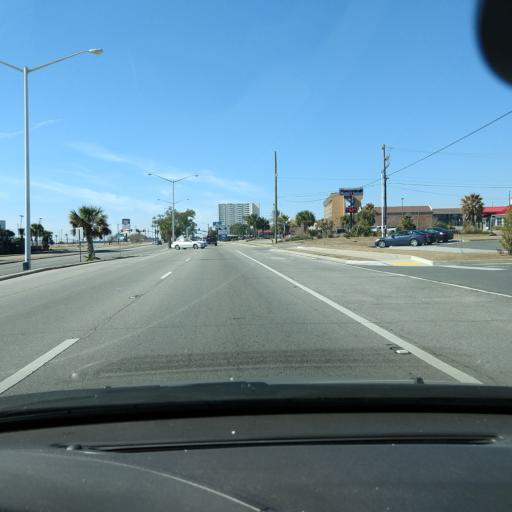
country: US
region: Mississippi
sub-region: Harrison County
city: Biloxi
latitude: 30.3934
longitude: -88.9509
